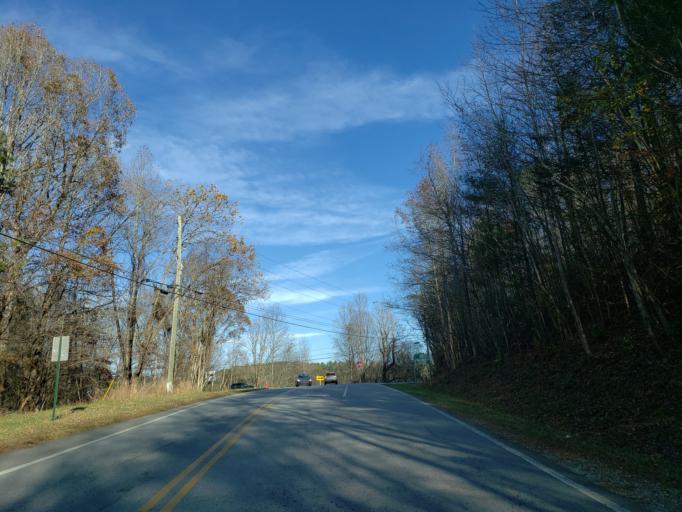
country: US
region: Georgia
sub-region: Lumpkin County
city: Dahlonega
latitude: 34.5501
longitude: -83.9964
